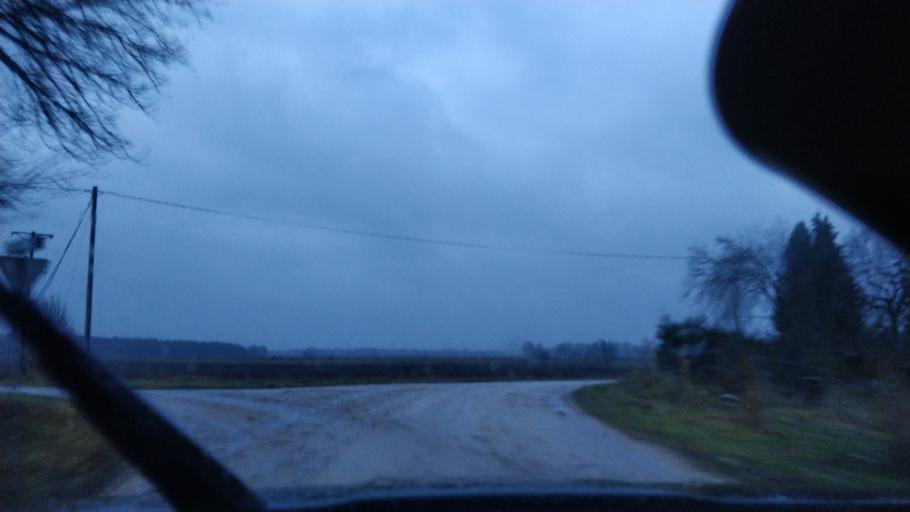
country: EE
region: Laeaene
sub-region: Lihula vald
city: Lihula
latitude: 58.8488
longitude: 23.9853
